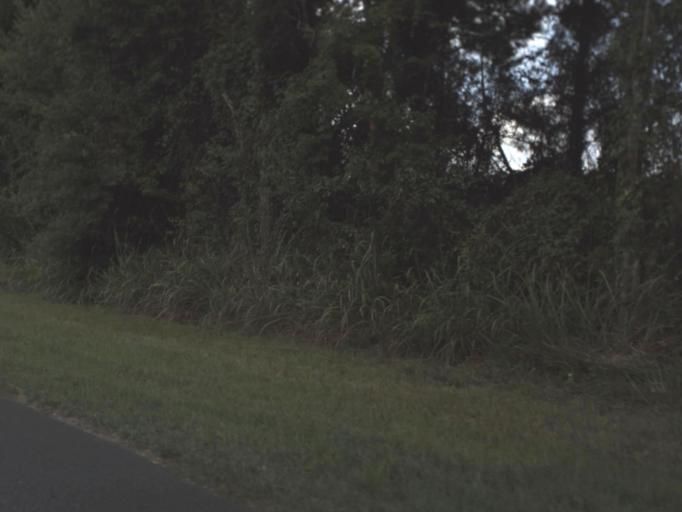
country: US
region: Florida
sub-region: Union County
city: Lake Butler
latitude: 29.9719
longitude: -82.4033
